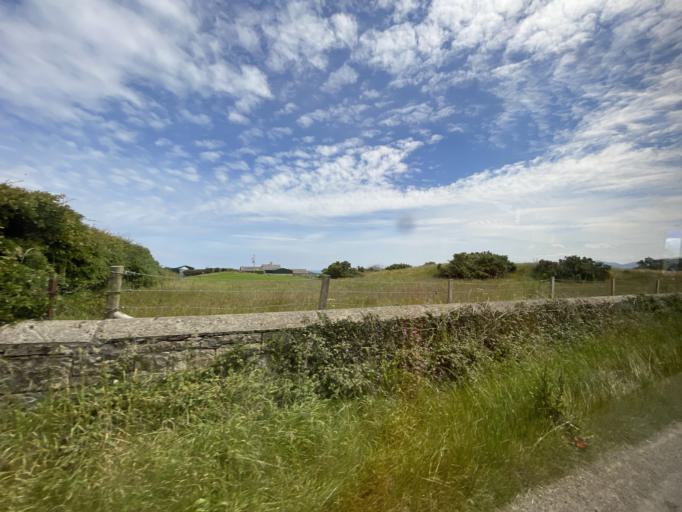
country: GB
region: Wales
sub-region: Anglesey
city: Beaumaris
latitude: 53.2811
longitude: -4.1266
